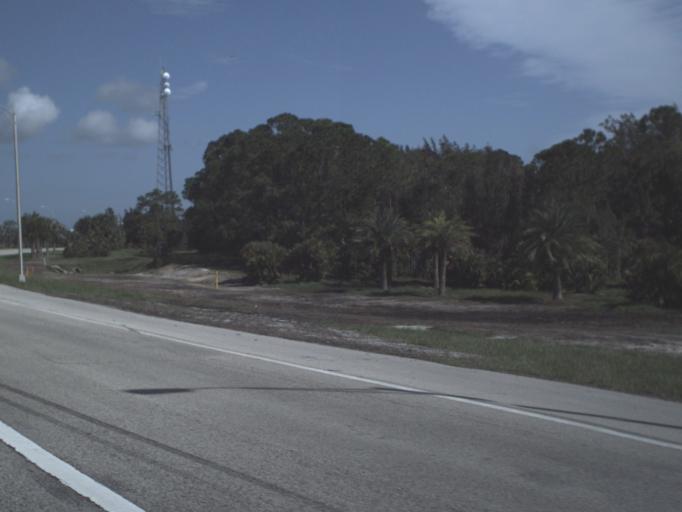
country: US
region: Florida
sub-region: Saint Lucie County
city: Fort Pierce South
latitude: 27.4051
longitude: -80.3989
